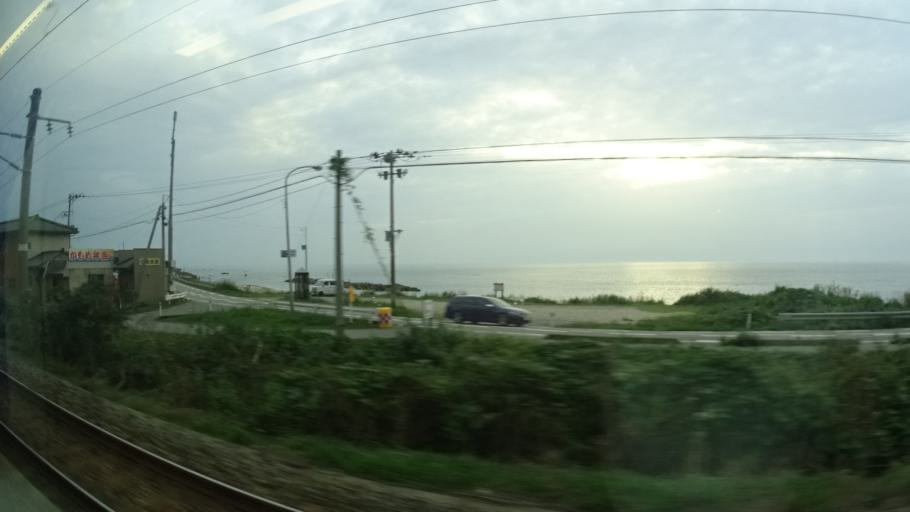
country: JP
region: Niigata
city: Murakami
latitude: 38.2630
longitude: 139.4474
